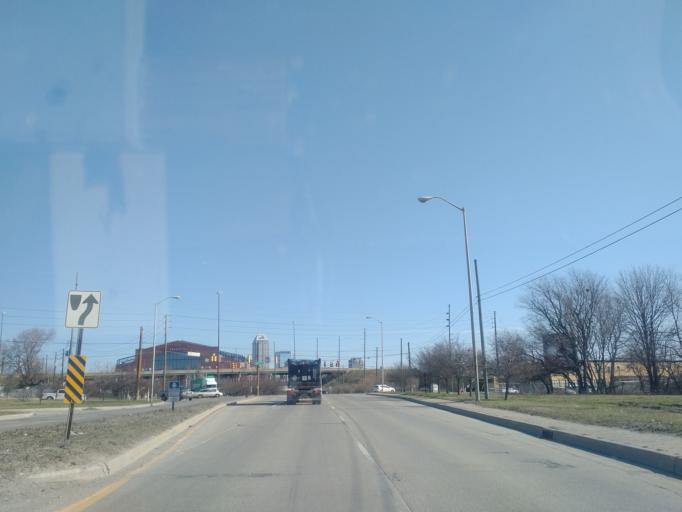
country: US
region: Indiana
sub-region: Marion County
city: Indianapolis
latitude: 39.7509
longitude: -86.1673
